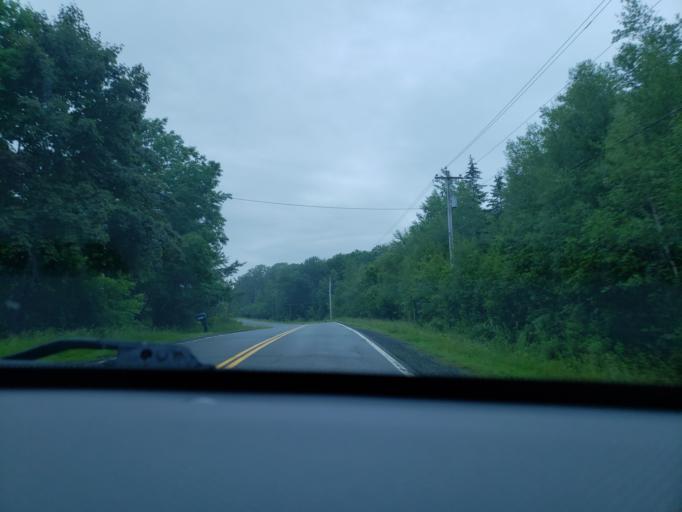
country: CA
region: Nova Scotia
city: Windsor
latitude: 45.0606
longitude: -63.9847
